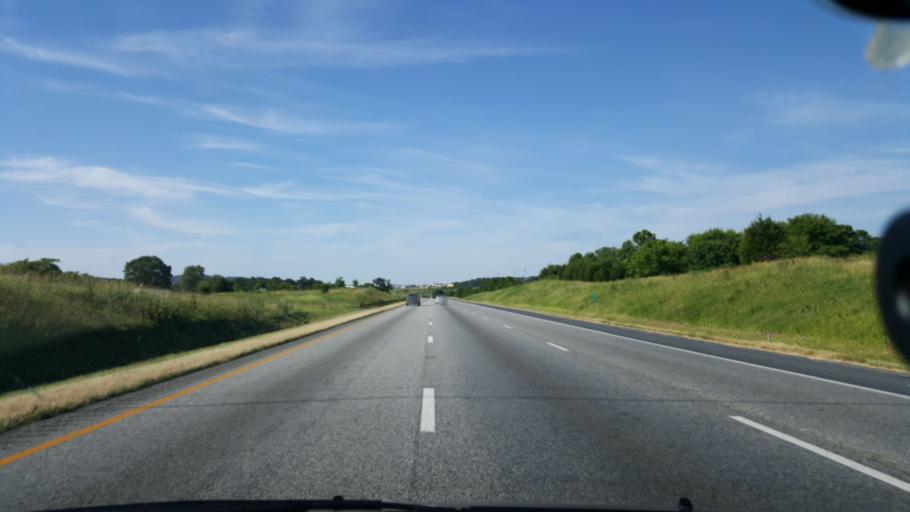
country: US
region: Virginia
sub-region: Rockingham County
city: Bridgewater
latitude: 38.3600
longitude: -78.9250
